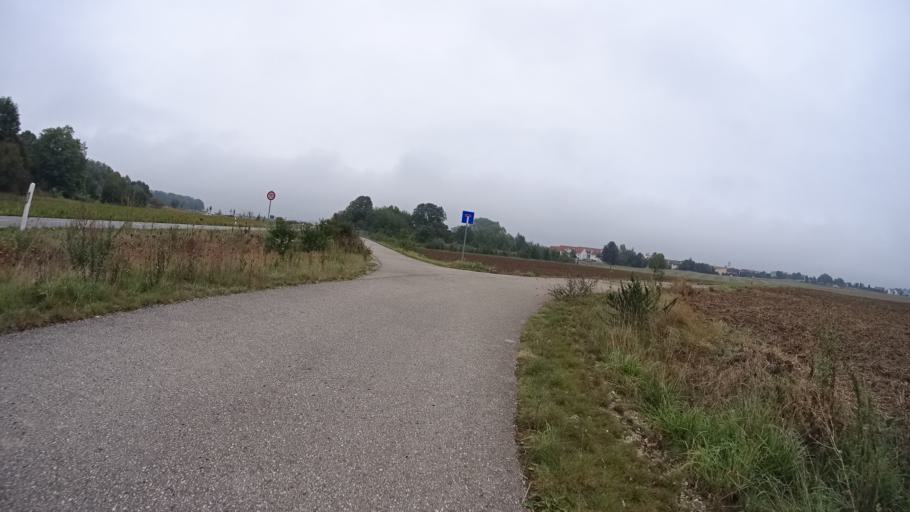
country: DE
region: Bavaria
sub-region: Upper Bavaria
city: Wettstetten
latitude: 48.8143
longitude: 11.4076
